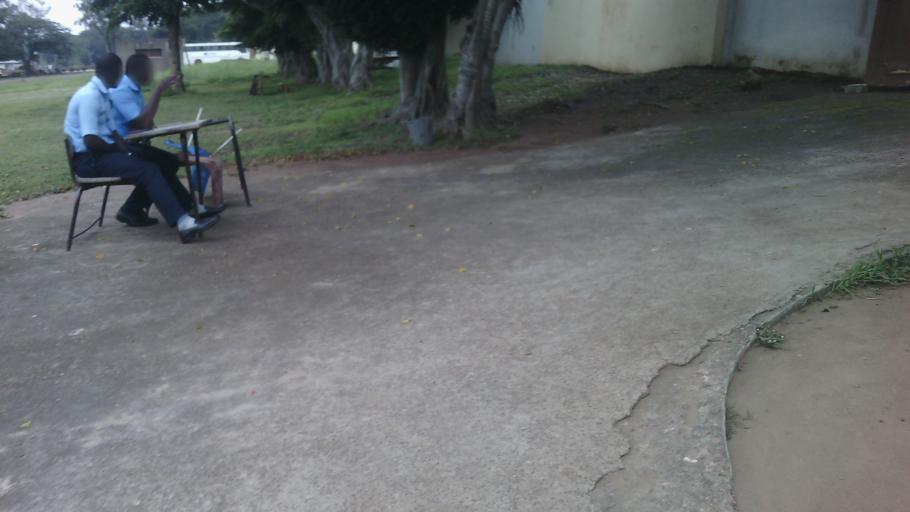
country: CI
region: Vallee du Bandama
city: Bouake
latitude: 7.6849
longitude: -5.0671
